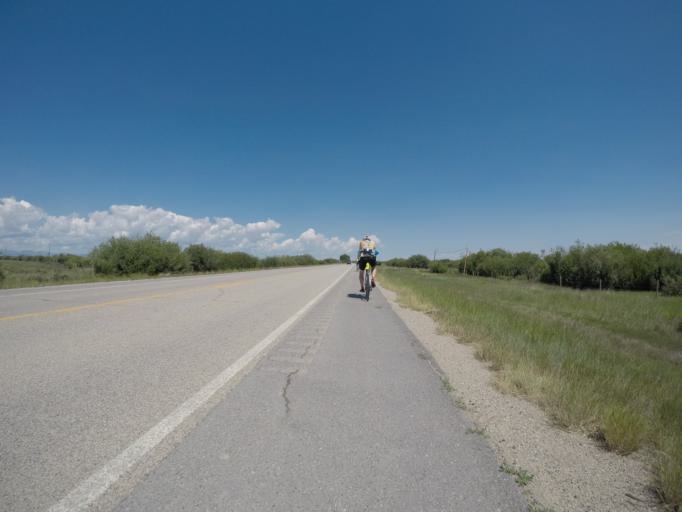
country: US
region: Wyoming
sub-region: Sublette County
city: Marbleton
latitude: 42.5208
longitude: -110.1065
